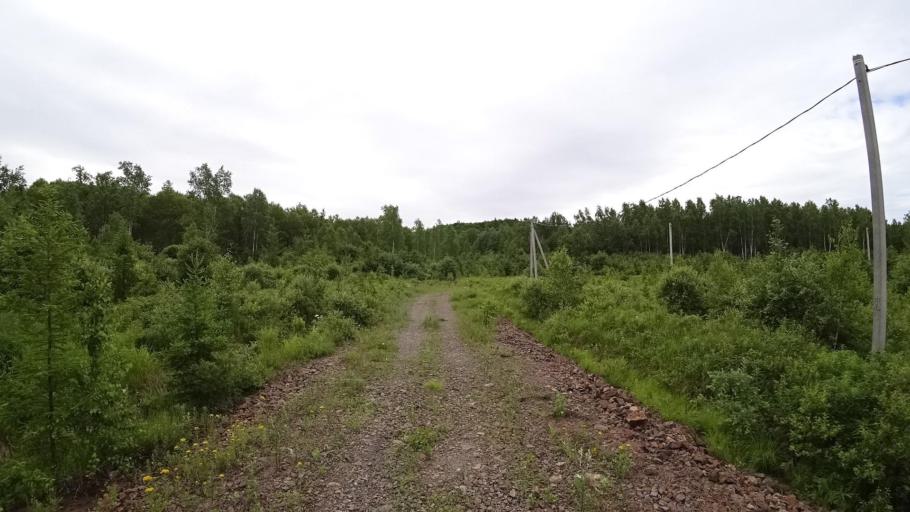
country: RU
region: Khabarovsk Krai
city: Amursk
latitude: 49.8985
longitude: 136.1654
